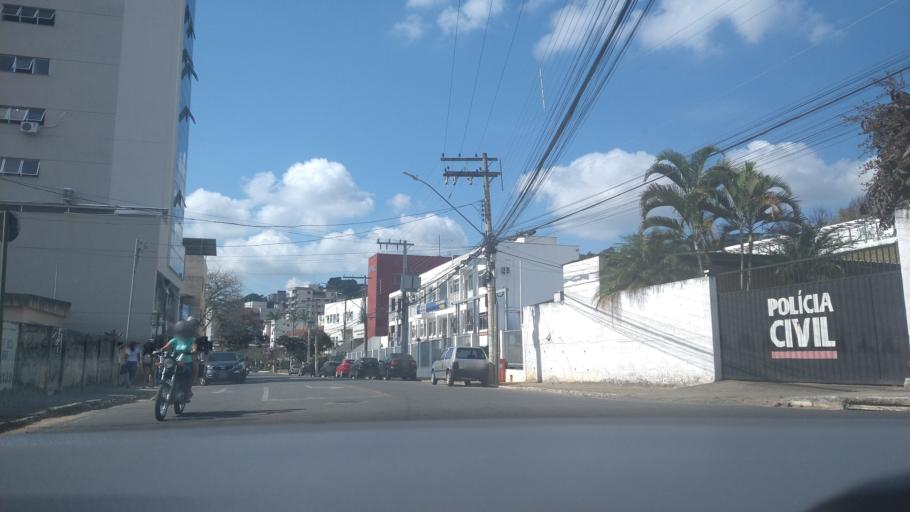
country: BR
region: Minas Gerais
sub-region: Vicosa
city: Vicosa
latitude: -20.7648
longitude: -42.8826
